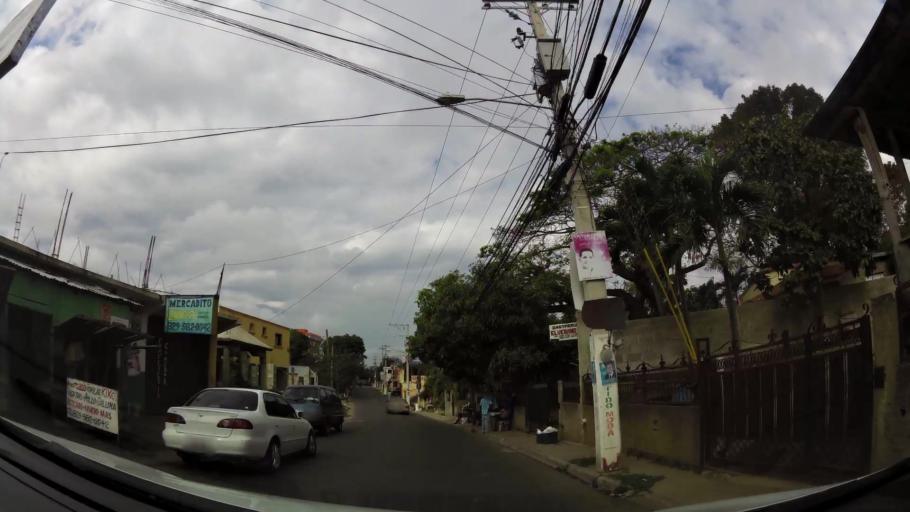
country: DO
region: Santiago
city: Santiago de los Caballeros
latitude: 19.4270
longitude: -70.6697
